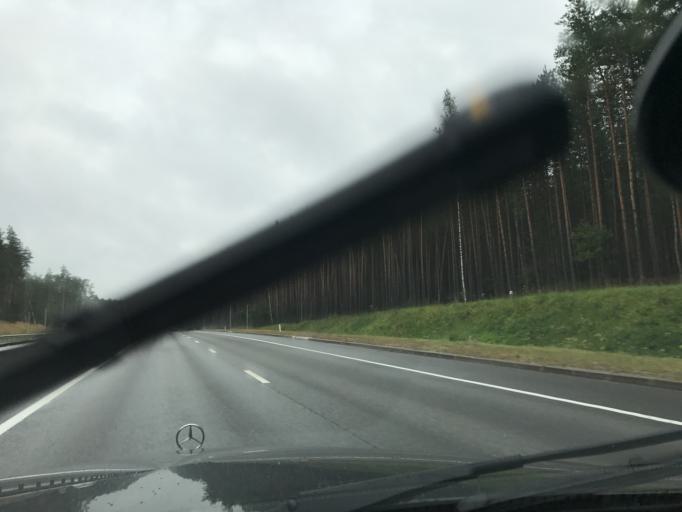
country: RU
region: Vladimir
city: Stepantsevo
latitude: 56.2236
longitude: 41.5785
